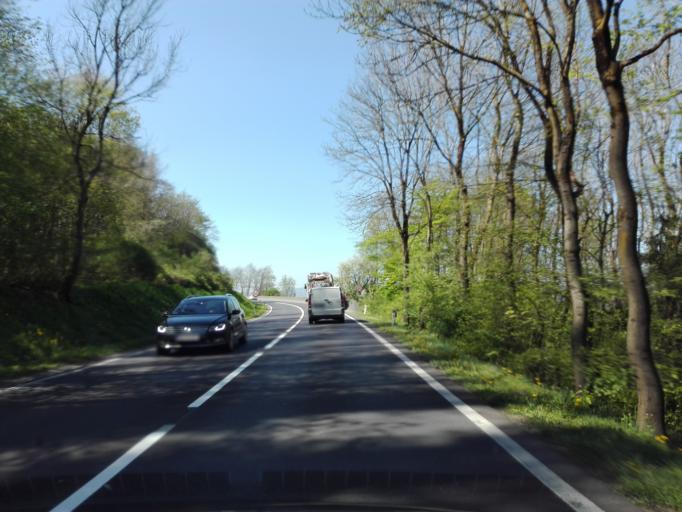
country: AT
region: Upper Austria
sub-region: Politischer Bezirk Urfahr-Umgebung
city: Steyregg
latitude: 48.2496
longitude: 14.3552
